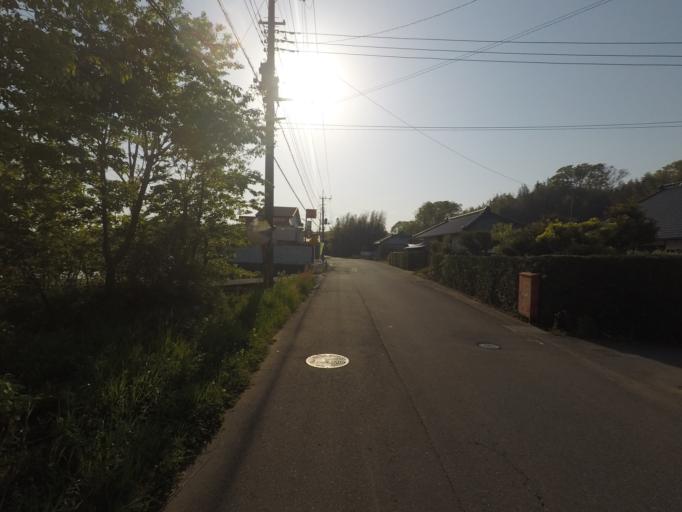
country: JP
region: Ibaraki
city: Ami
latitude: 36.0715
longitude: 140.3085
